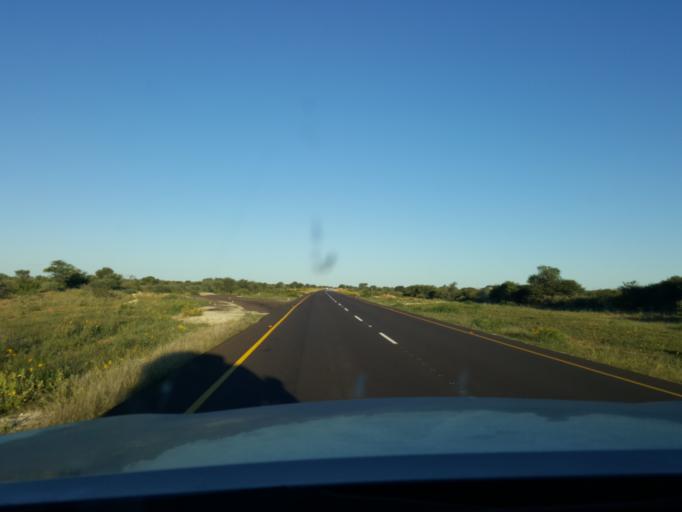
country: BW
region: Southern
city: Sekoma
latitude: -24.4468
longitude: 23.7648
